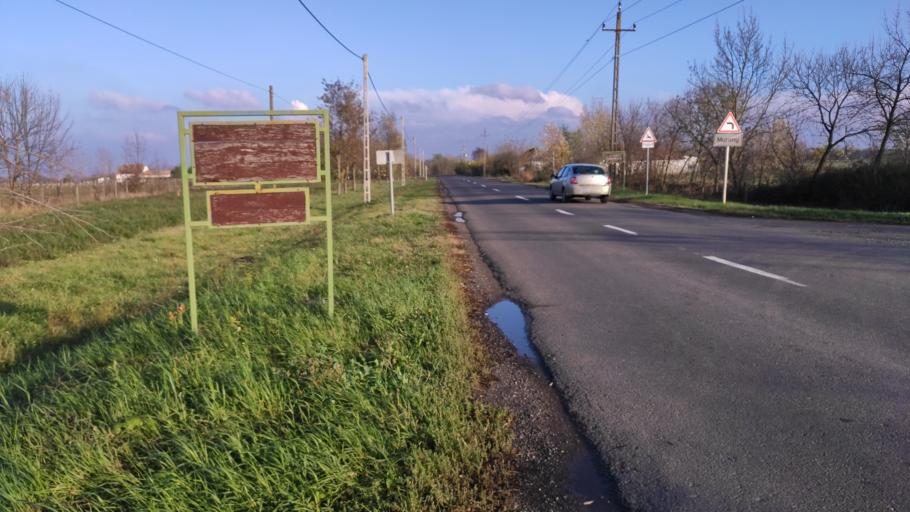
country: HU
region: Bekes
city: Mezobereny
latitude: 46.7610
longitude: 21.0483
